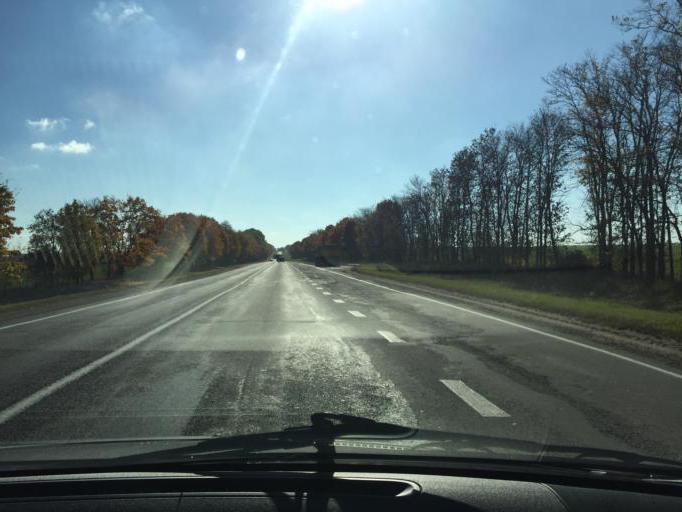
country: BY
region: Minsk
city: Salihorsk
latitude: 52.8916
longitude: 27.4725
